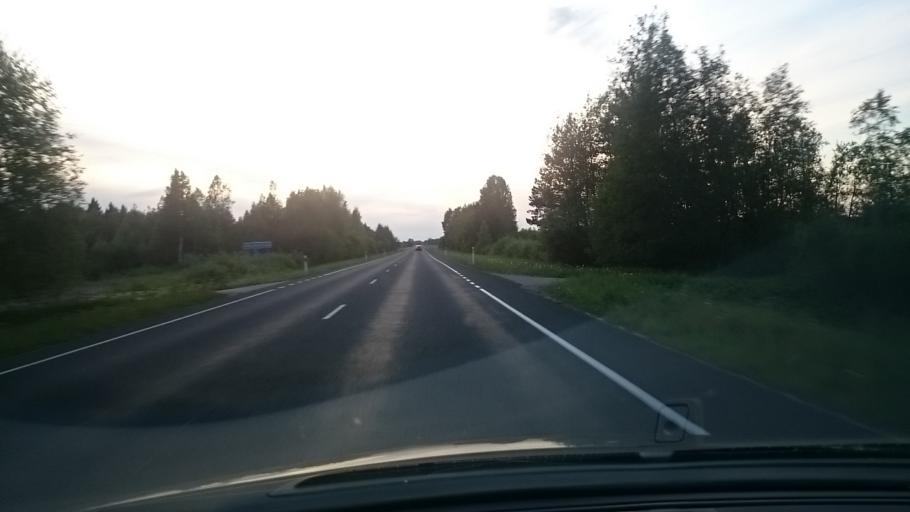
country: EE
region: Viljandimaa
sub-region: Vohma linn
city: Vohma
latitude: 58.7426
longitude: 25.5795
